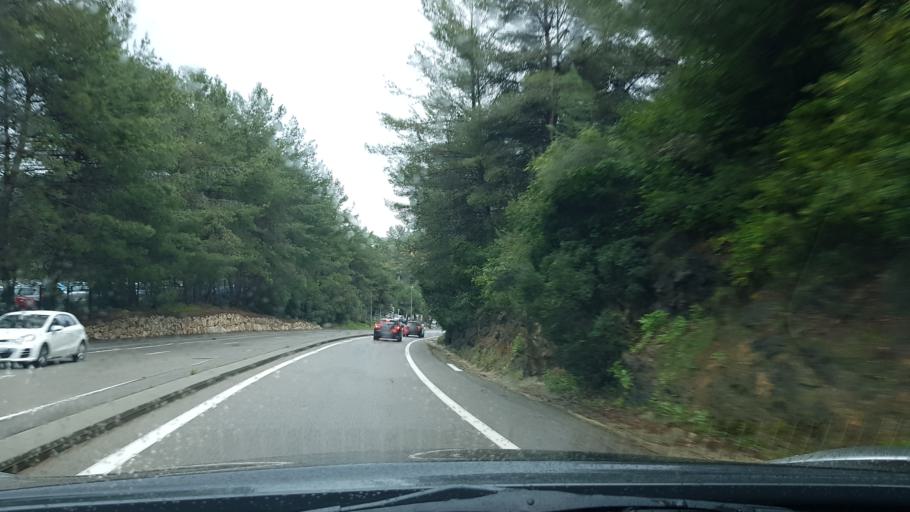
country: FR
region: Provence-Alpes-Cote d'Azur
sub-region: Departement des Alpes-Maritimes
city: Valbonne
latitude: 43.6219
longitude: 7.0341
